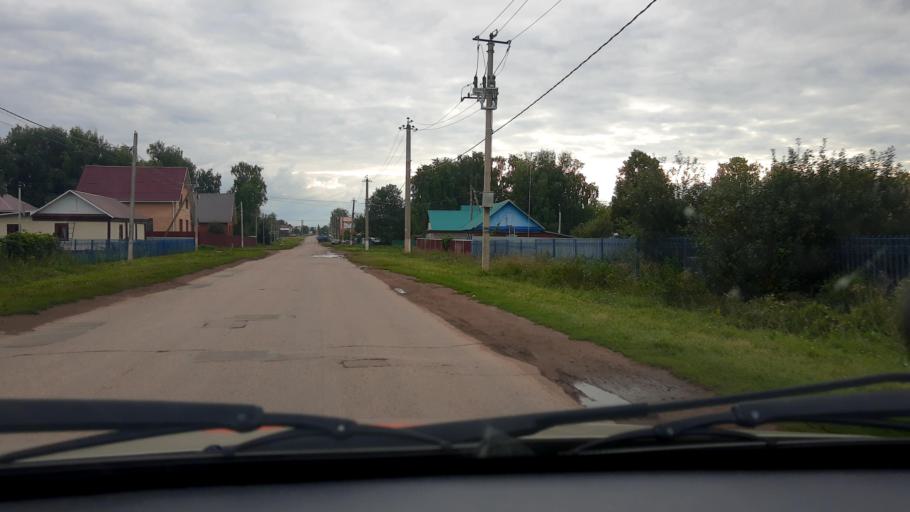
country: RU
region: Bashkortostan
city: Chishmy
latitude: 54.5947
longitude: 55.3889
